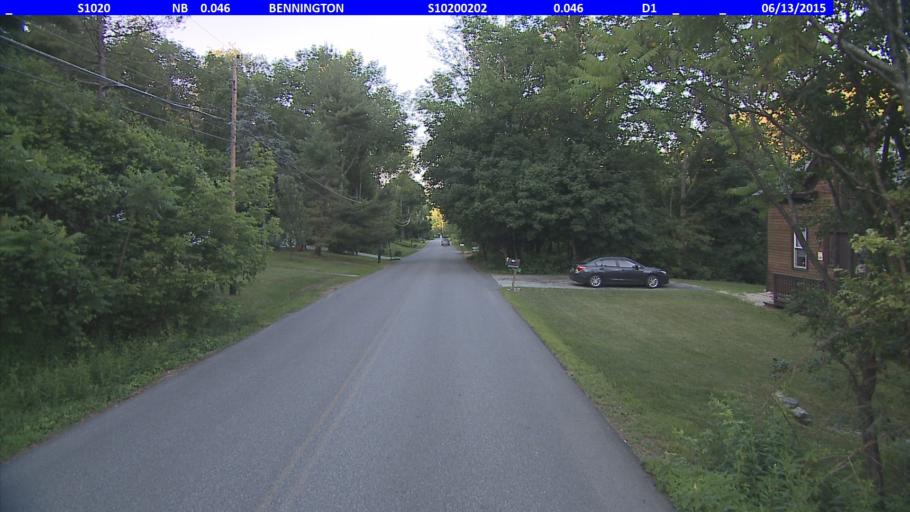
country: US
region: Vermont
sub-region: Bennington County
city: Bennington
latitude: 42.8676
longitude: -73.2087
